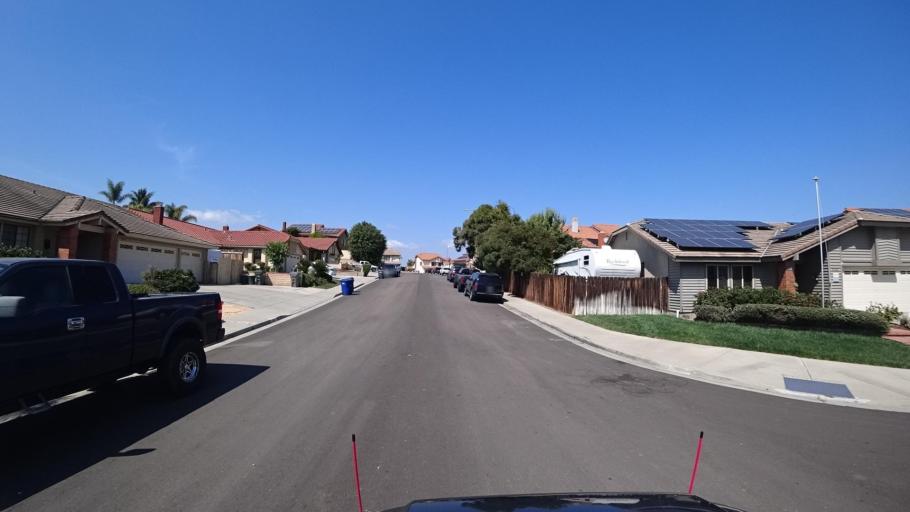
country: US
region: California
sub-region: San Diego County
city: Spring Valley
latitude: 32.7430
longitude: -116.9896
